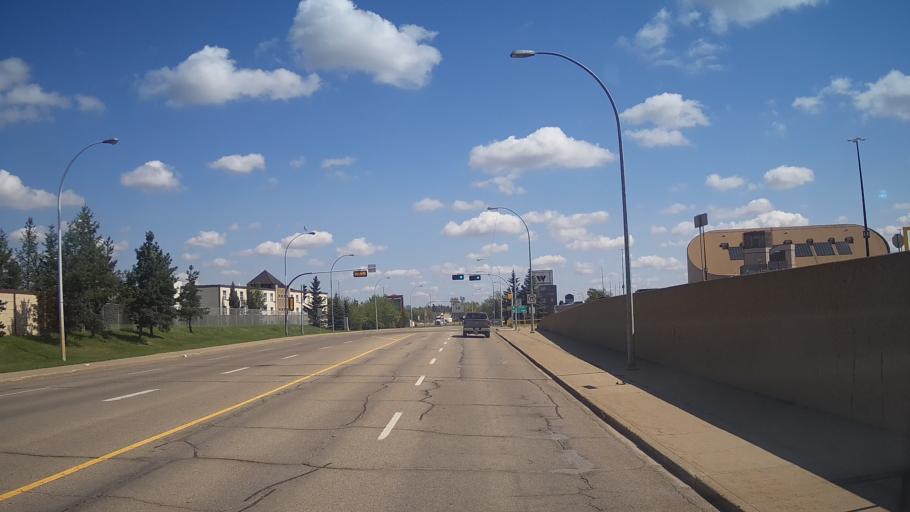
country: CA
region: Alberta
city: St. Albert
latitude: 53.5248
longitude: -113.6265
